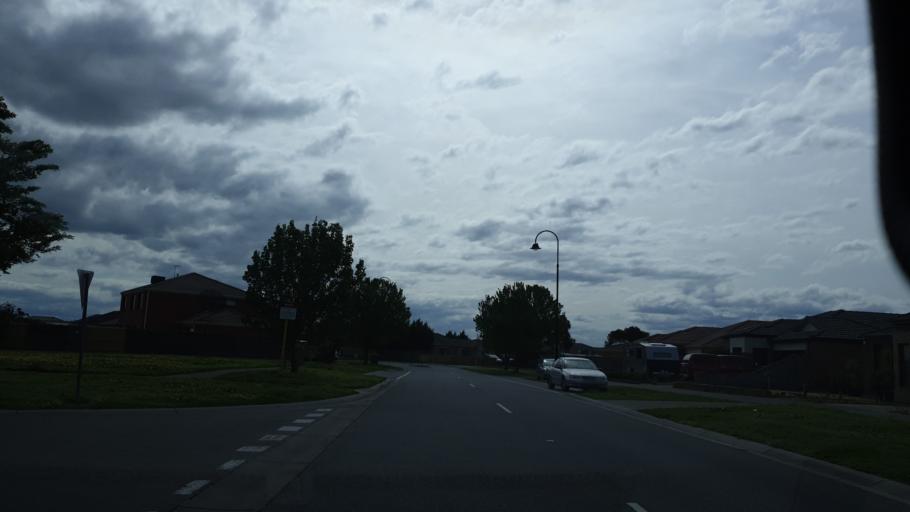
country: AU
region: Victoria
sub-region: Casey
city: Cranbourne North
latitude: -38.0769
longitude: 145.2952
